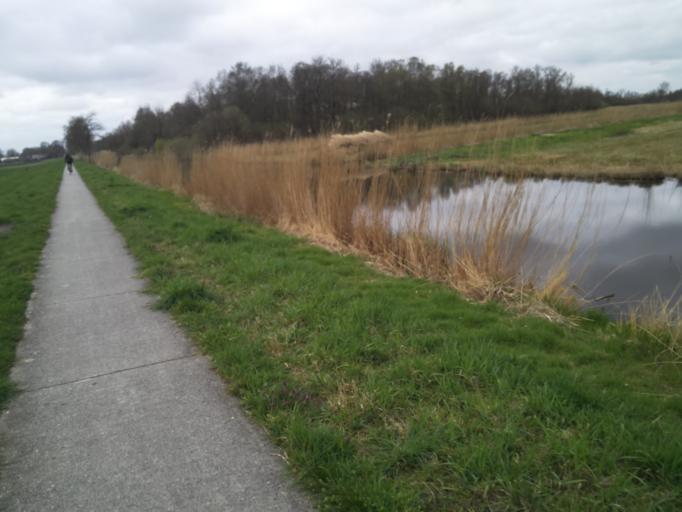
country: NL
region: Overijssel
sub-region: Gemeente Steenwijkerland
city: Giethoorn
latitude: 52.7373
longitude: 6.0519
